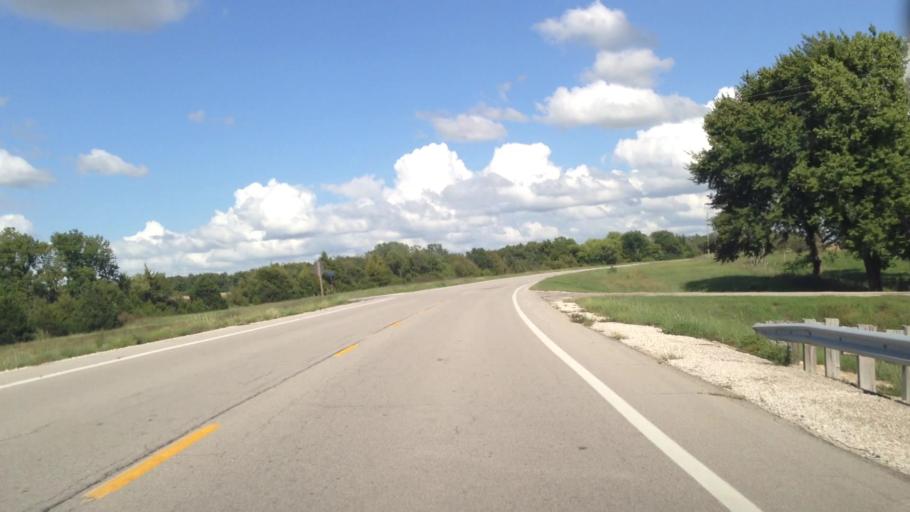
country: US
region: Kansas
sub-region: Neosho County
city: Erie
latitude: 37.6879
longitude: -95.2349
